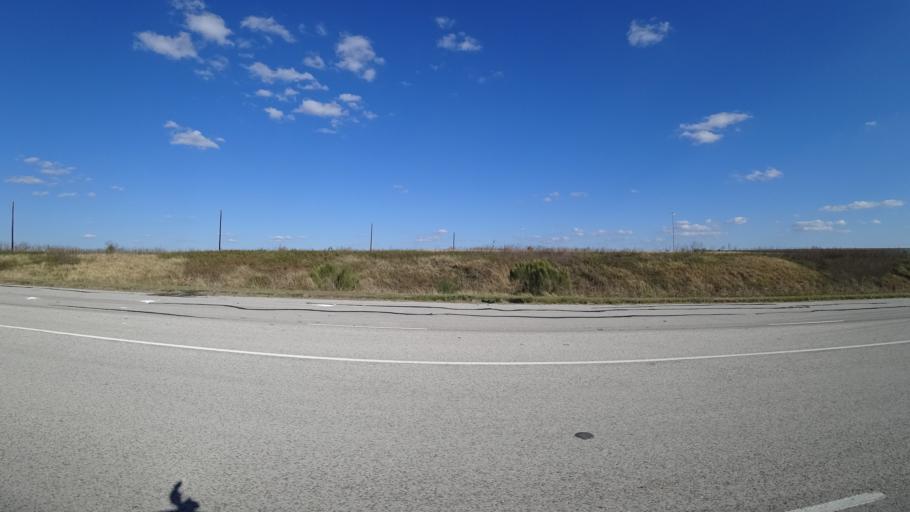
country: US
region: Texas
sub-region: Travis County
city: Onion Creek
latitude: 30.0838
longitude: -97.6921
